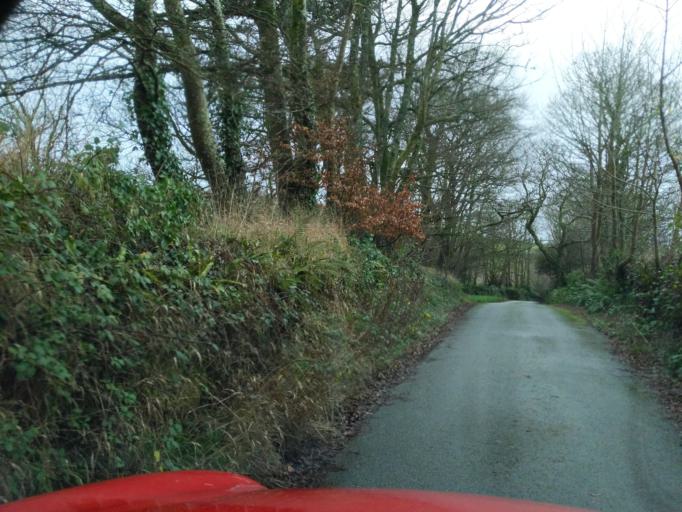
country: GB
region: England
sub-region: Cornwall
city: Duloe
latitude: 50.3519
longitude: -4.5123
